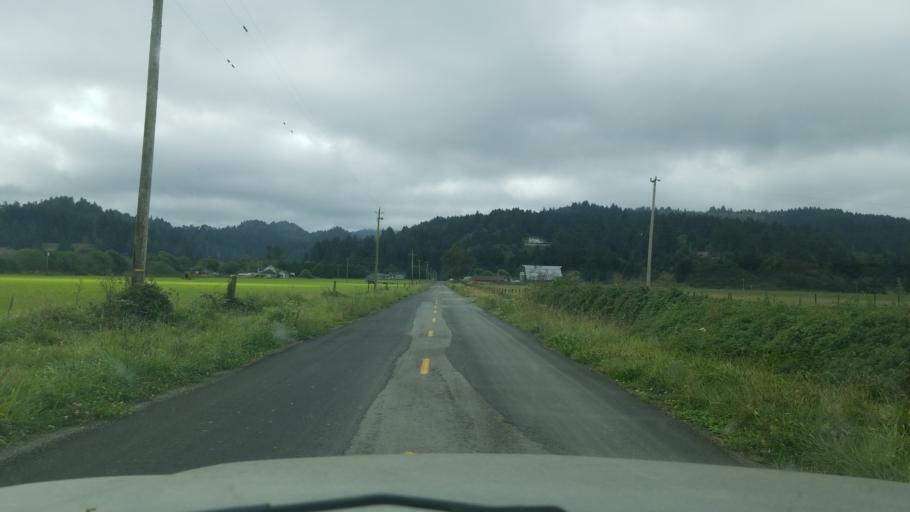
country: US
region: California
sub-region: Humboldt County
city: Ferndale
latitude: 40.5885
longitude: -124.2839
